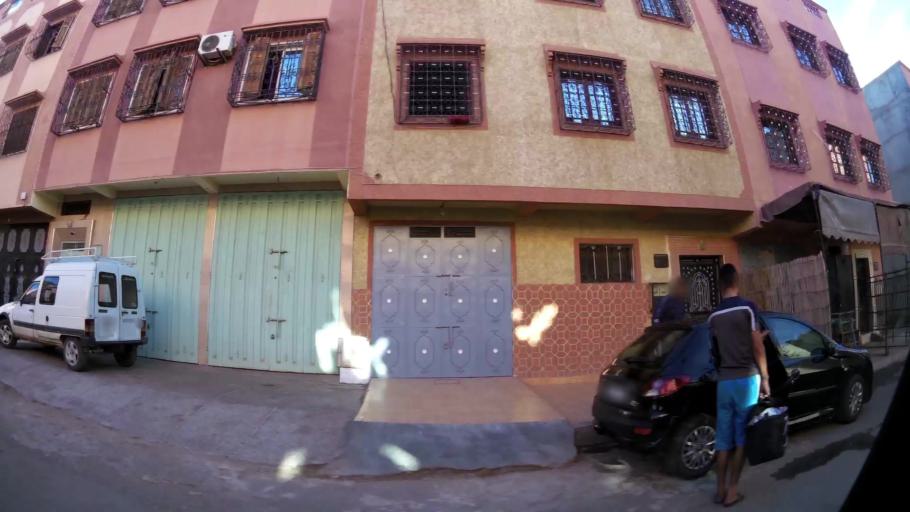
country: MA
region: Marrakech-Tensift-Al Haouz
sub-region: Marrakech
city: Marrakesh
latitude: 31.6162
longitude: -8.0689
